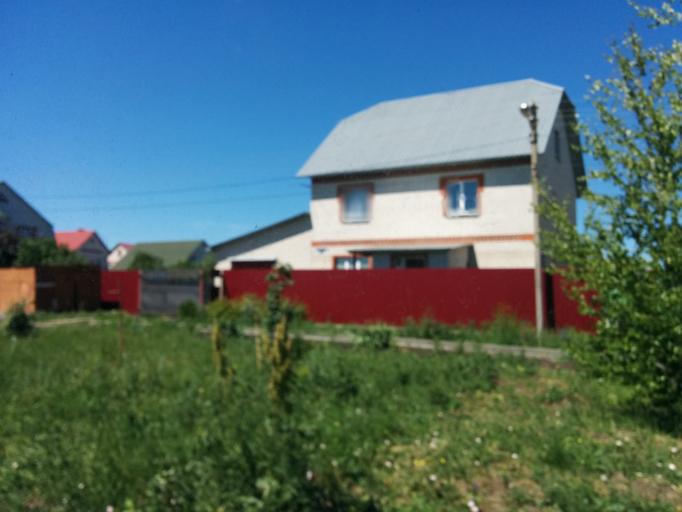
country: RU
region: Tambov
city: Tambov
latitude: 52.7791
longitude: 41.3823
